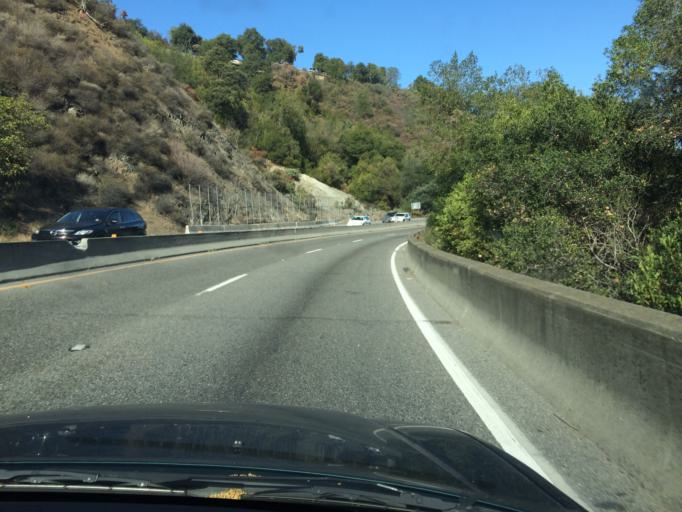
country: US
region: California
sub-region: Santa Clara County
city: Los Gatos
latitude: 37.2104
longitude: -121.9898
